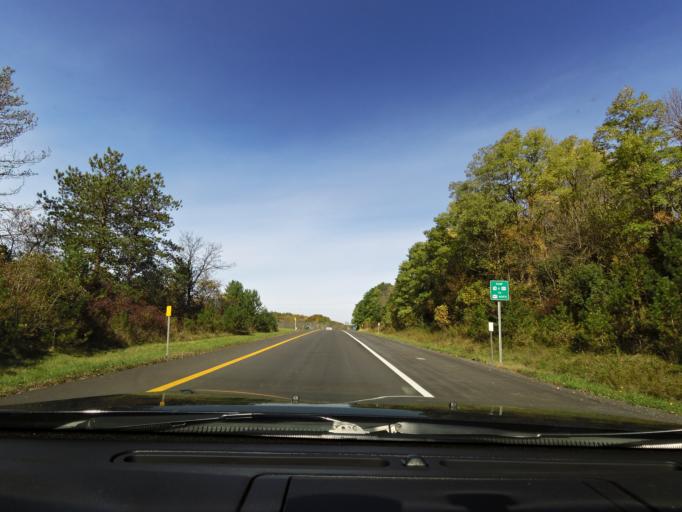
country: US
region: New York
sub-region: Erie County
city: East Aurora
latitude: 42.7682
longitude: -78.5925
